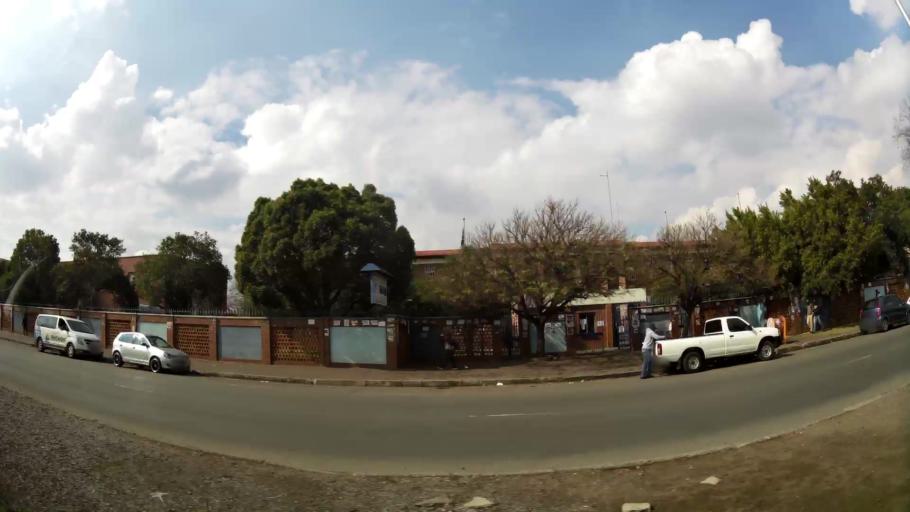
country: ZA
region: Gauteng
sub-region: Sedibeng District Municipality
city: Vereeniging
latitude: -26.6782
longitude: 27.9308
